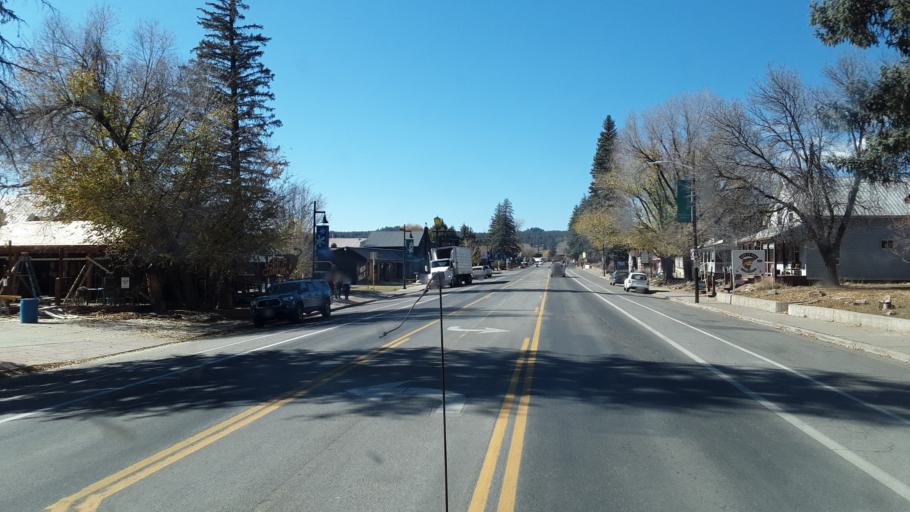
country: US
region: Colorado
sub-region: Archuleta County
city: Pagosa Springs
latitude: 37.2690
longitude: -107.0029
